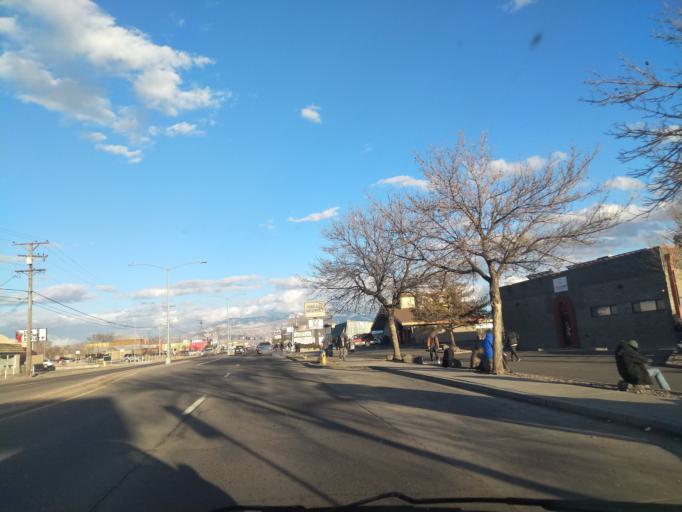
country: US
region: Colorado
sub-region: Mesa County
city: Fruitvale
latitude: 39.0773
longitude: -108.5232
